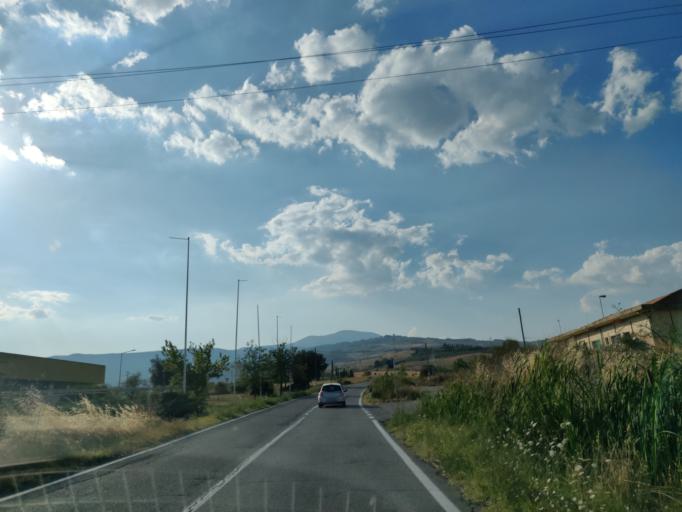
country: IT
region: Tuscany
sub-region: Provincia di Siena
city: Piancastagnaio
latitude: 42.8249
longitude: 11.7254
